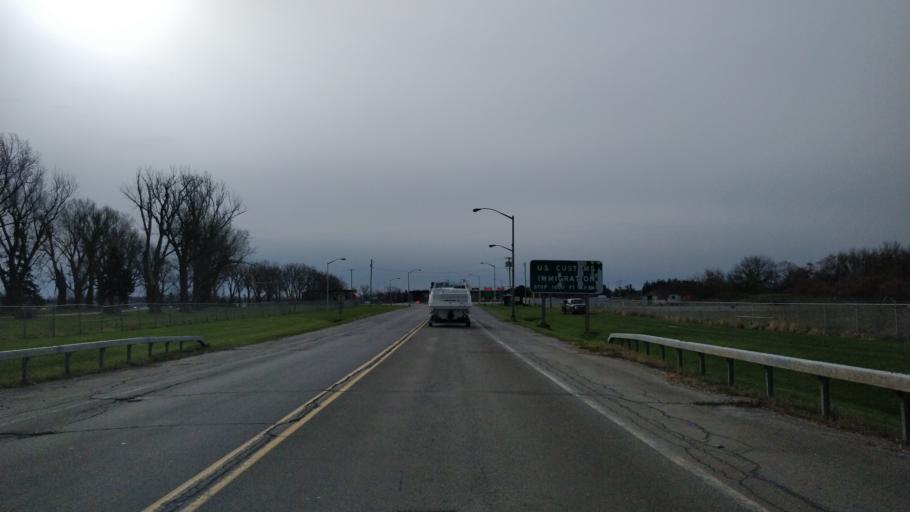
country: US
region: New York
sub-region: St. Lawrence County
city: Ogdensburg
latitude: 44.7254
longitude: -75.4551
